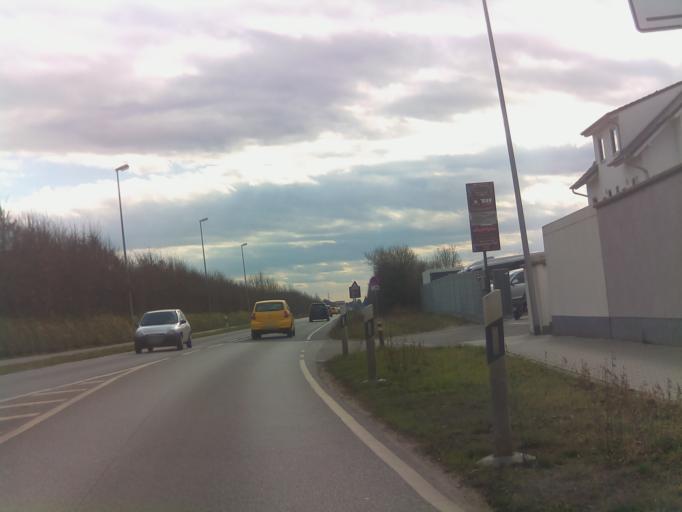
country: DE
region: Hesse
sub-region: Regierungsbezirk Darmstadt
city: Gross-Gerau
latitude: 49.8988
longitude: 8.4802
